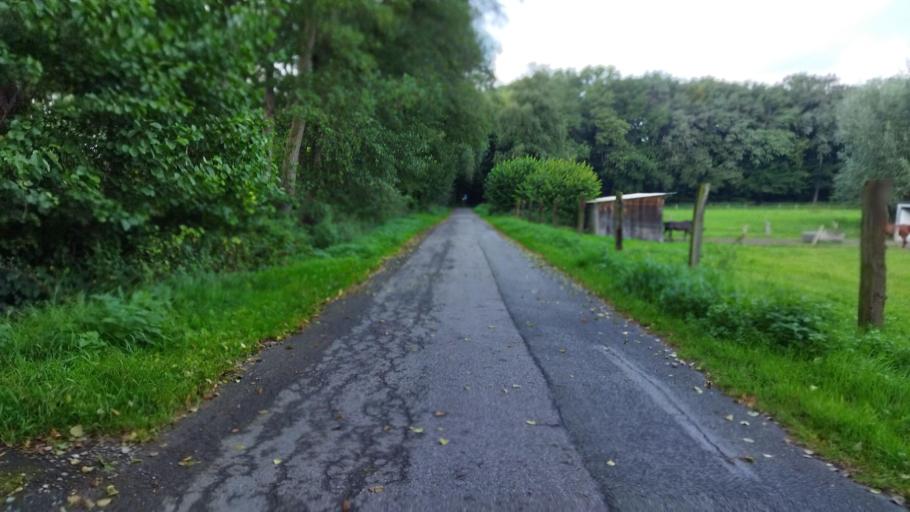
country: DE
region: North Rhine-Westphalia
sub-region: Regierungsbezirk Munster
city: Warendorf
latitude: 51.9611
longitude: 7.9314
